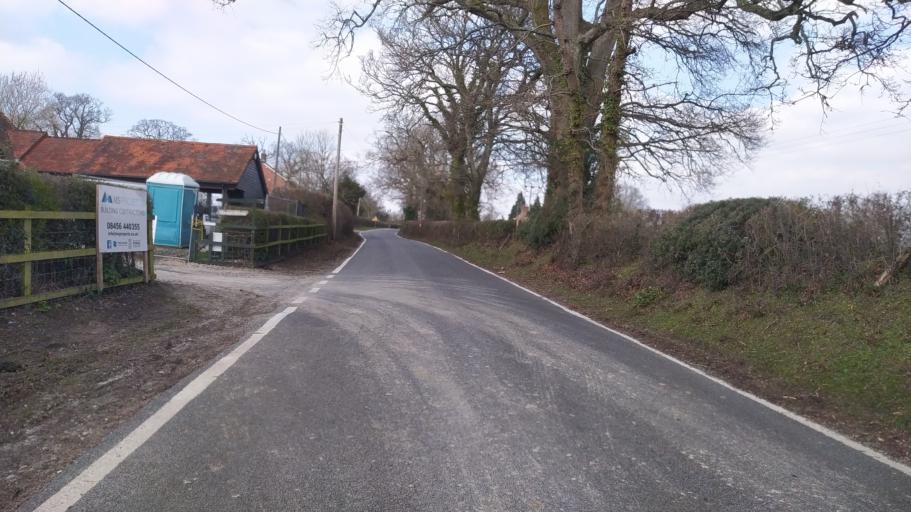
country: GB
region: England
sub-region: Hampshire
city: Cadnam
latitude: 50.9358
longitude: -1.6168
